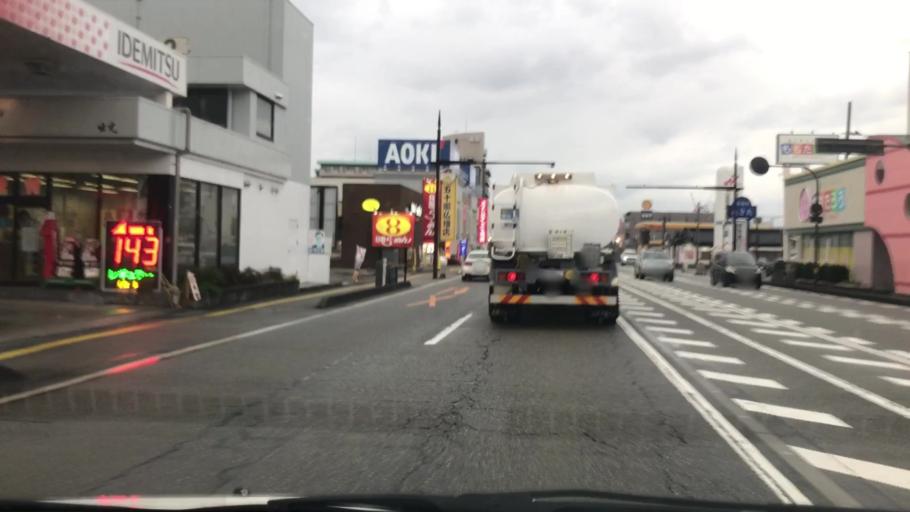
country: JP
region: Toyama
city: Toyama-shi
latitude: 36.6750
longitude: 137.2107
